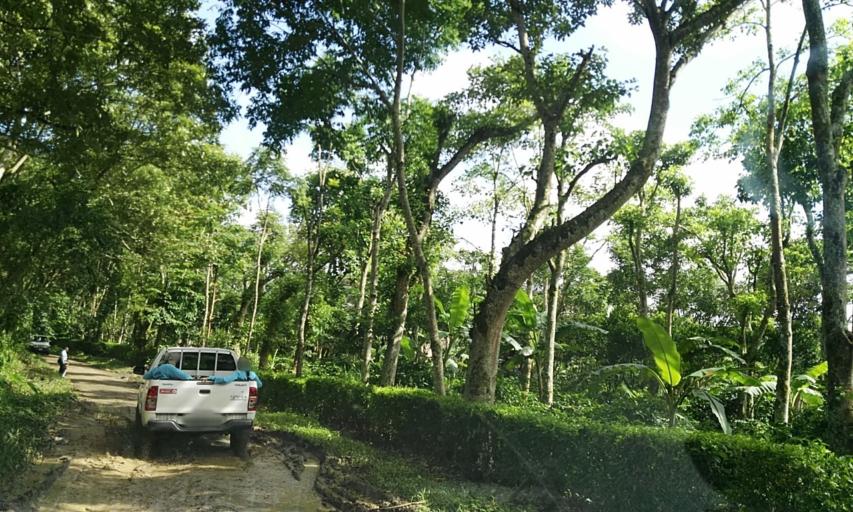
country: NI
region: Matagalpa
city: San Ramon
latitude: 12.9855
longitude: -85.8465
